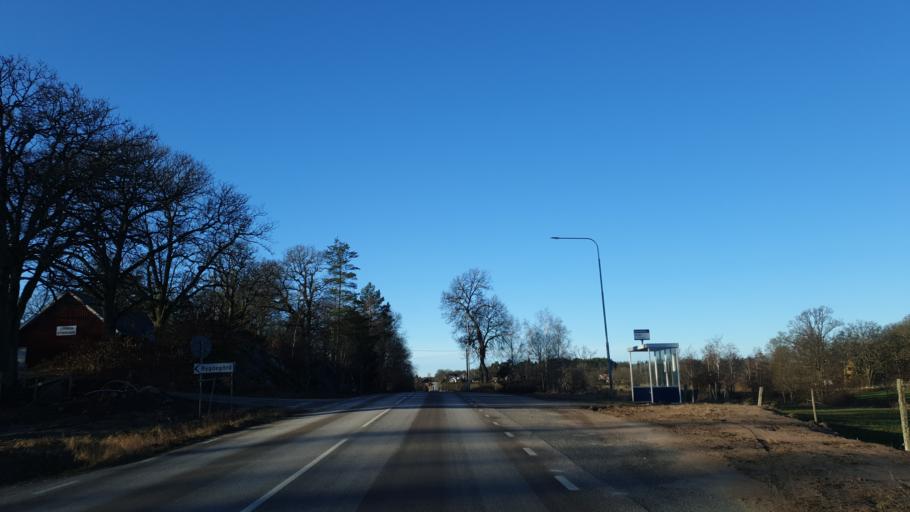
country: SE
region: Blekinge
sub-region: Ronneby Kommun
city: Ronneby
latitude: 56.1937
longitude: 15.3468
